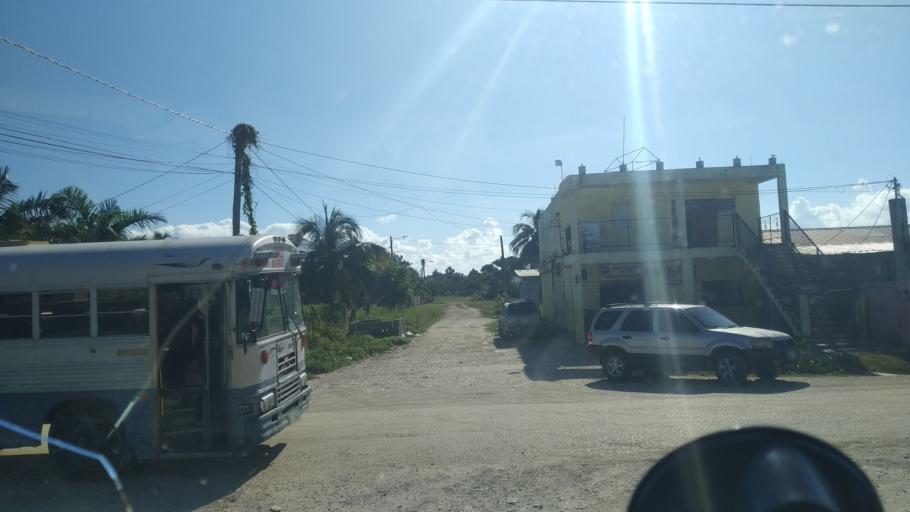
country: BZ
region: Belize
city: Belize City
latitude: 17.5505
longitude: -88.3244
